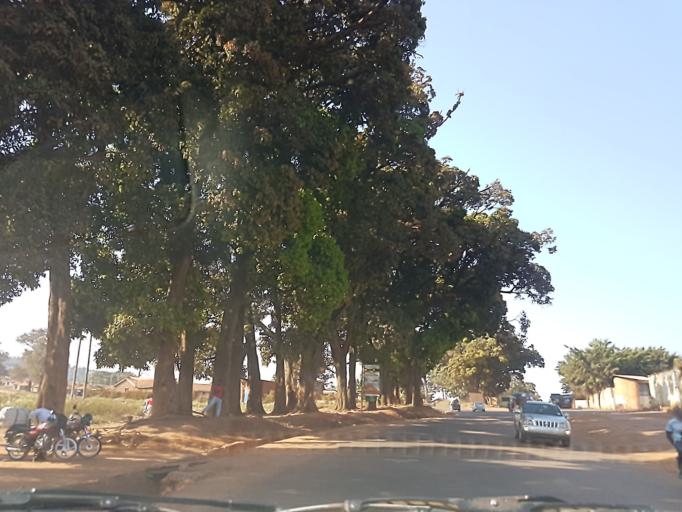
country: UG
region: Central Region
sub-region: Wakiso District
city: Kireka
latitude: 0.3362
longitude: 32.6151
